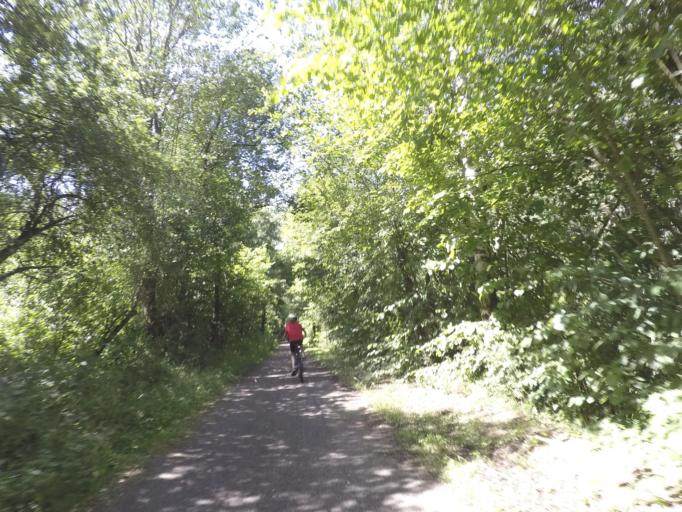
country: BE
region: Wallonia
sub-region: Province de Liege
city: Modave
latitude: 50.4436
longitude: 5.3198
